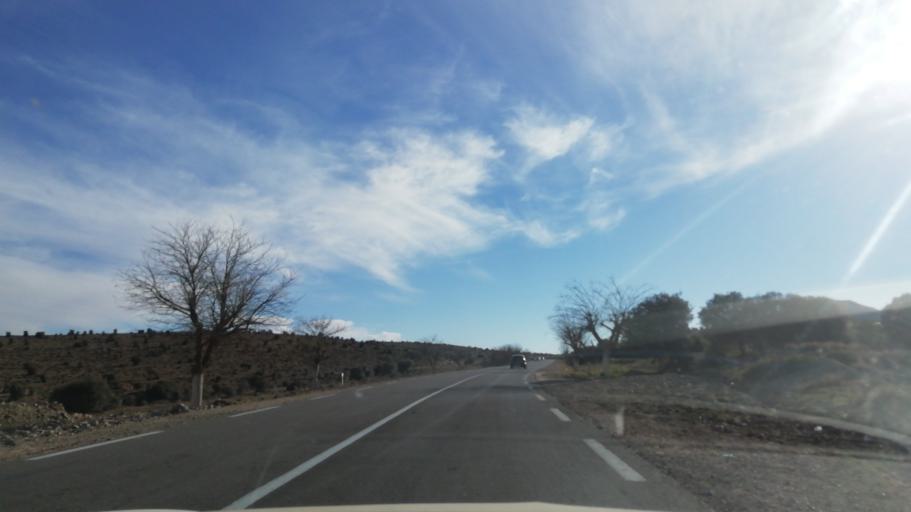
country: DZ
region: Tlemcen
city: Sebdou
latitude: 34.5866
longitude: -1.3176
